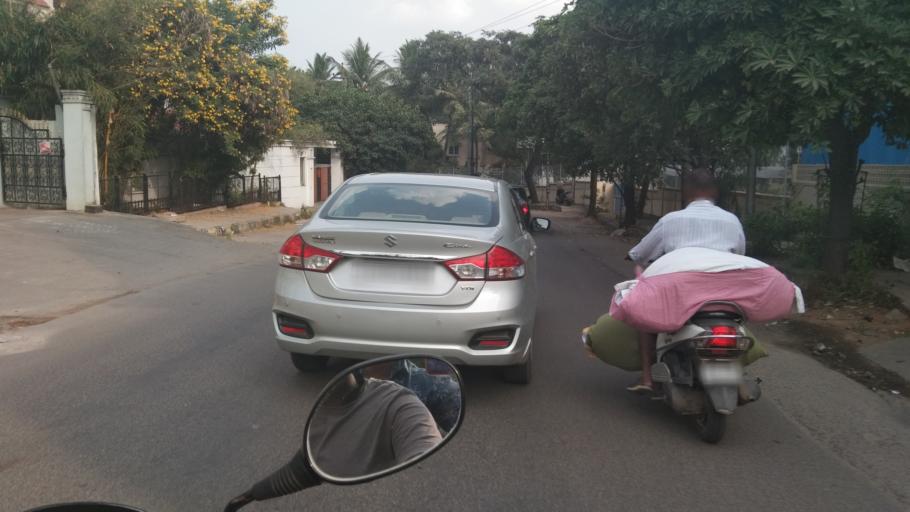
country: IN
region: Telangana
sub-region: Rangareddi
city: Kukatpalli
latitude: 17.4313
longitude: 78.4212
